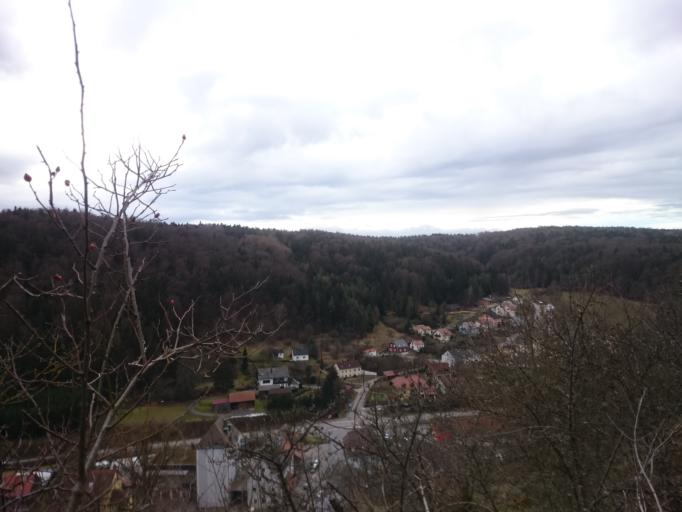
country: DE
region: Bavaria
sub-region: Upper Palatinate
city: Kallmunz
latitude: 49.1619
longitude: 11.9520
